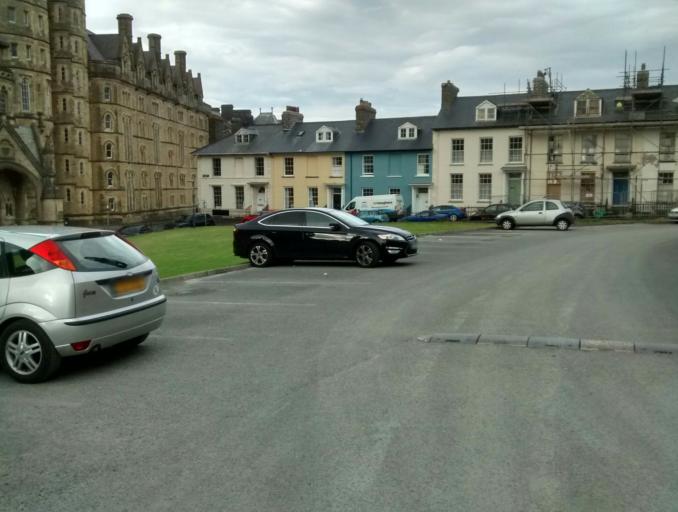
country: GB
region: Wales
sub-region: County of Ceredigion
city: Aberystwyth
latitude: 52.4142
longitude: -4.0886
